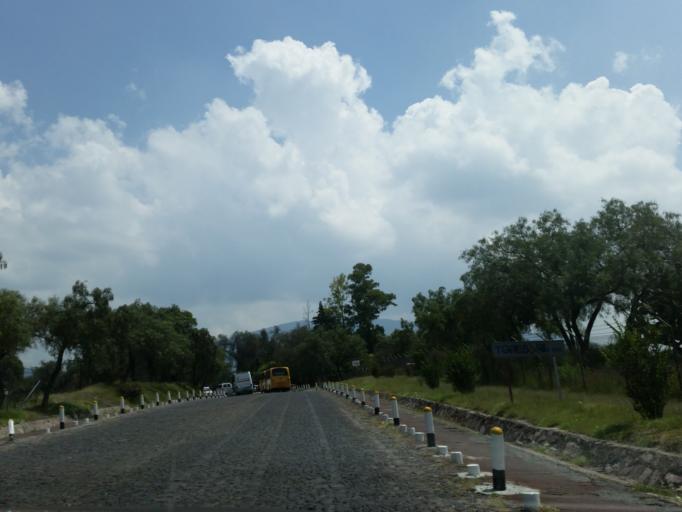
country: MX
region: Mexico
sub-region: Teotihuacan
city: Teotihuacan de Arista
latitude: 19.6925
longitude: -98.8496
